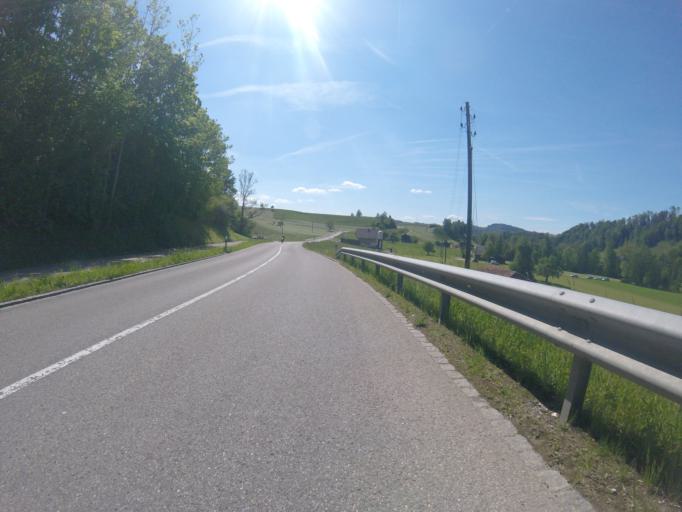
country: CH
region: Saint Gallen
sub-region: Wahlkreis Toggenburg
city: Ganterschwil
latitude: 47.3825
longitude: 9.1041
